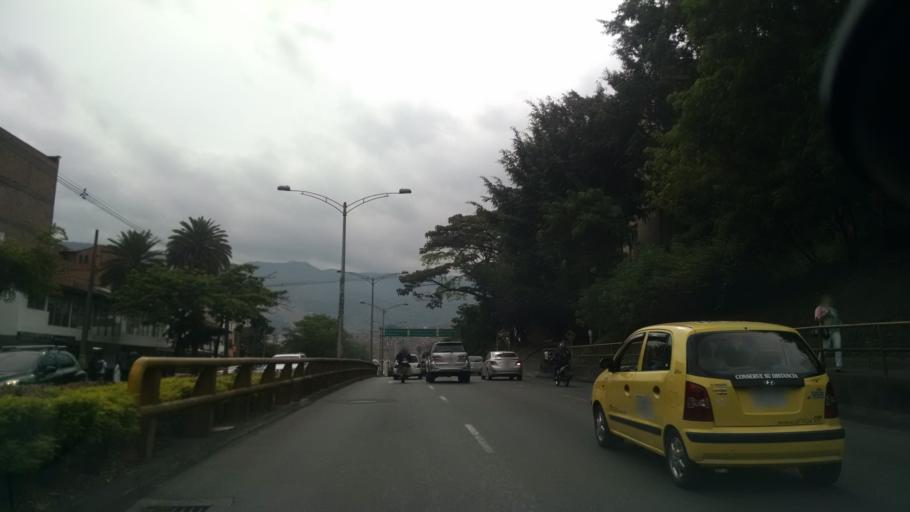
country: CO
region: Antioquia
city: Medellin
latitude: 6.2395
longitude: -75.5805
